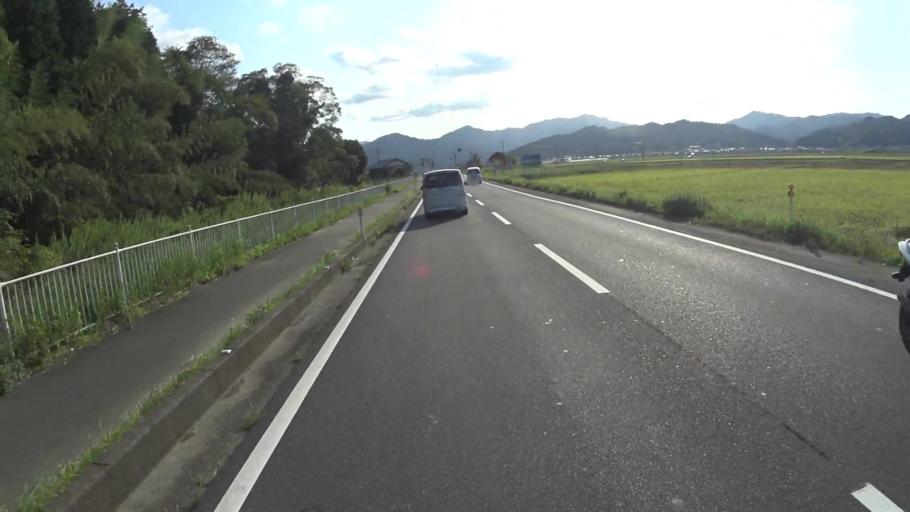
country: JP
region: Kyoto
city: Miyazu
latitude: 35.5214
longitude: 135.1104
